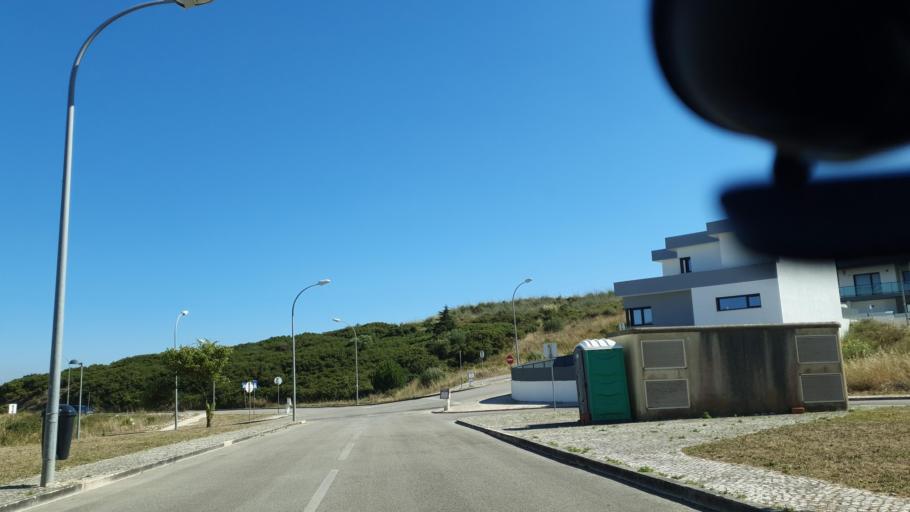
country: PT
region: Lisbon
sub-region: Odivelas
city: Canecas
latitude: 38.8053
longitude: -9.2526
